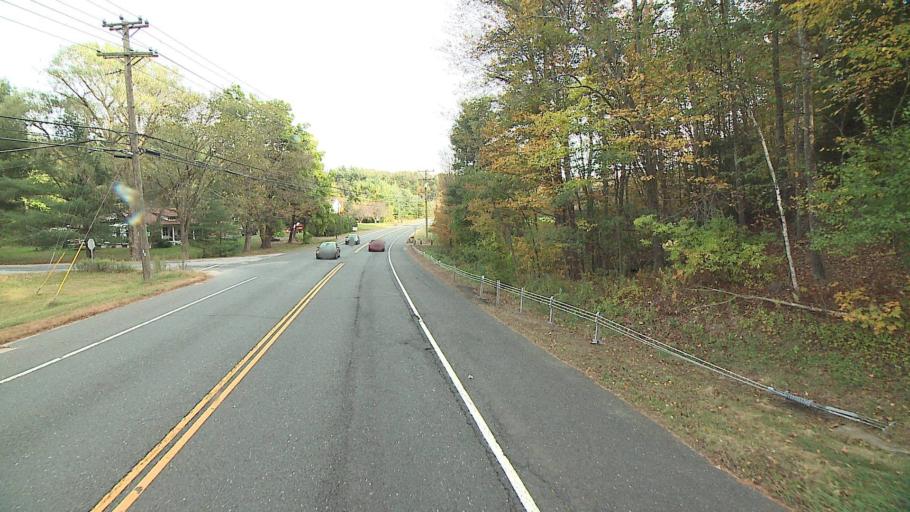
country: US
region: Connecticut
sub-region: Litchfield County
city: New Hartford Center
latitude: 41.8538
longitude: -72.9529
